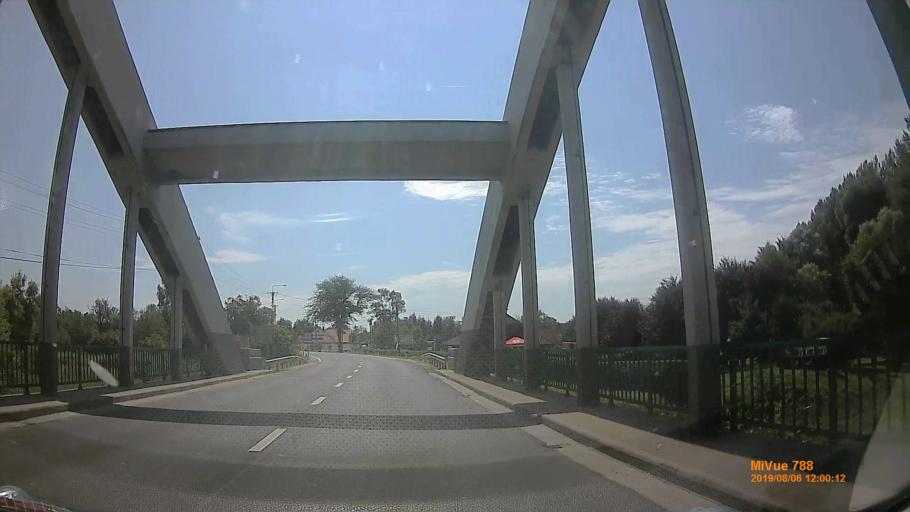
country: HU
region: Vas
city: Vasvar
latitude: 47.0635
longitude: 16.7457
